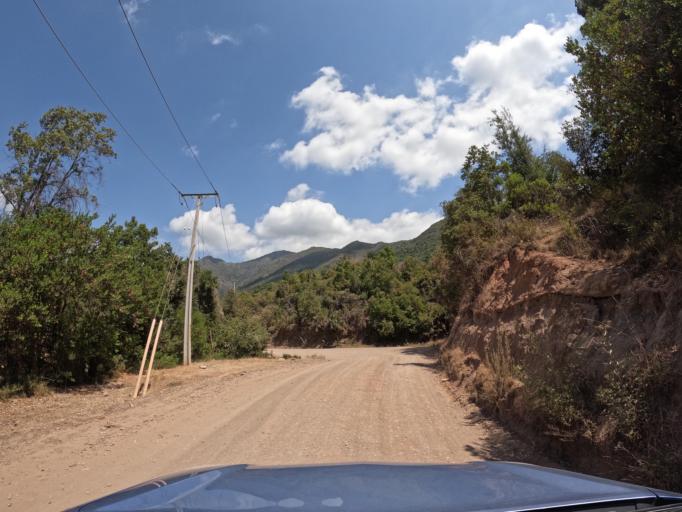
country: CL
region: Maule
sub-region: Provincia de Curico
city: Curico
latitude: -35.1191
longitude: -71.0079
